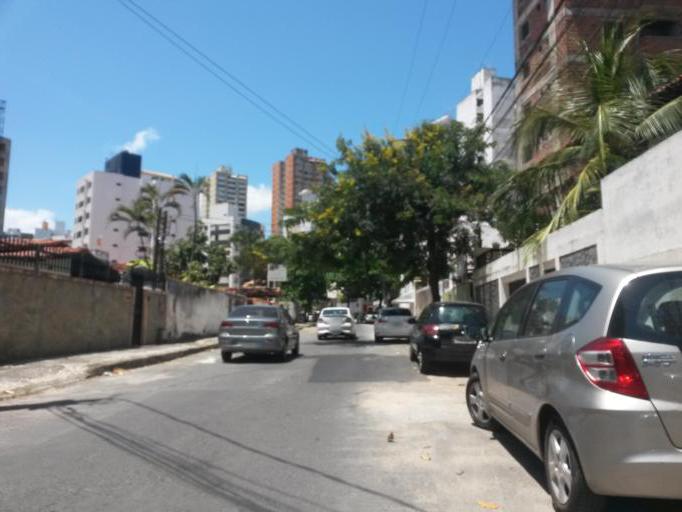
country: BR
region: Bahia
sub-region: Salvador
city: Salvador
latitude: -13.0026
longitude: -38.4624
